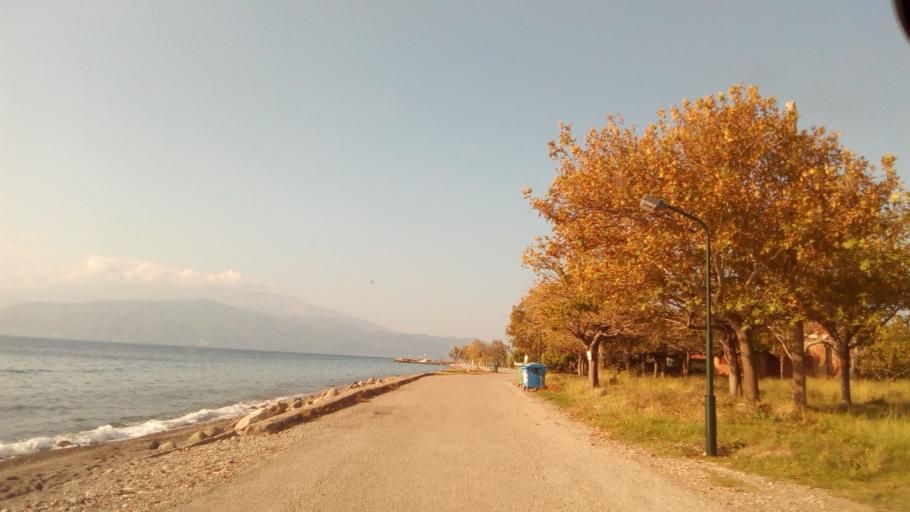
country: GR
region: West Greece
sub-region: Nomos Achaias
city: Kamarai
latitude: 38.3936
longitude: 22.0177
